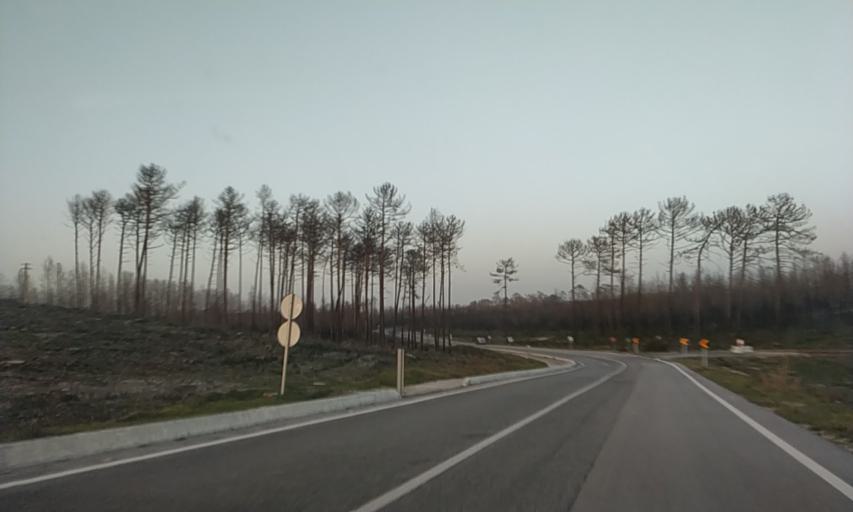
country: PT
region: Leiria
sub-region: Marinha Grande
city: Marinha Grande
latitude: 39.7438
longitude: -8.9804
